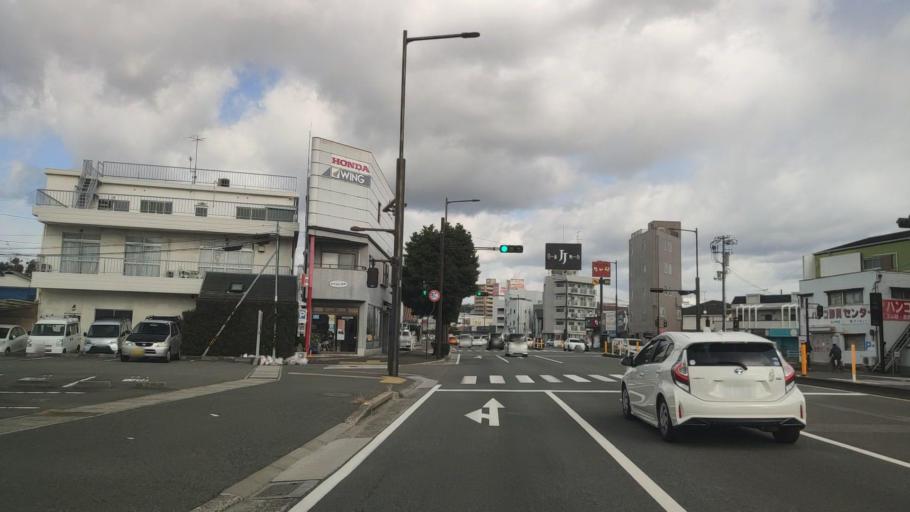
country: JP
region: Ehime
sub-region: Shikoku-chuo Shi
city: Matsuyama
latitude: 33.8249
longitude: 132.7582
